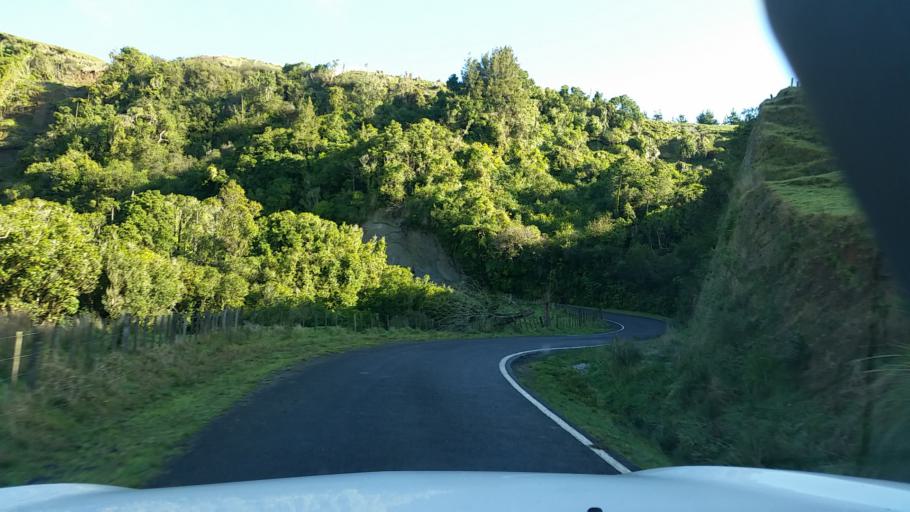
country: NZ
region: Taranaki
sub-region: South Taranaki District
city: Eltham
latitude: -39.5118
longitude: 174.3831
